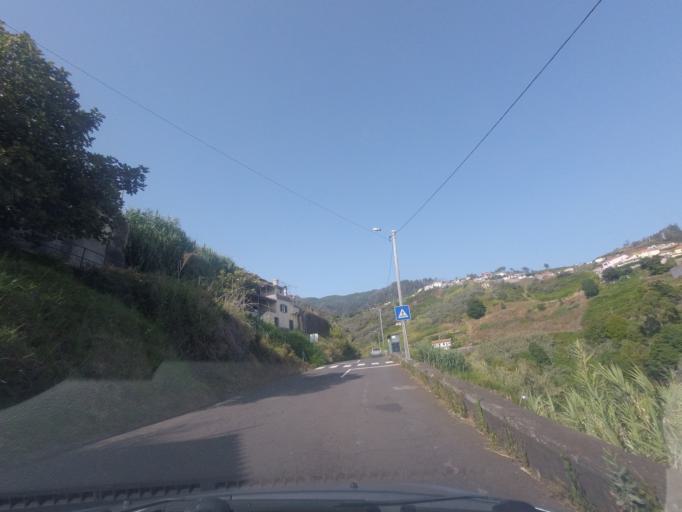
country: PT
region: Madeira
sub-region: Calheta
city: Arco da Calheta
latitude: 32.7298
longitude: -17.1551
